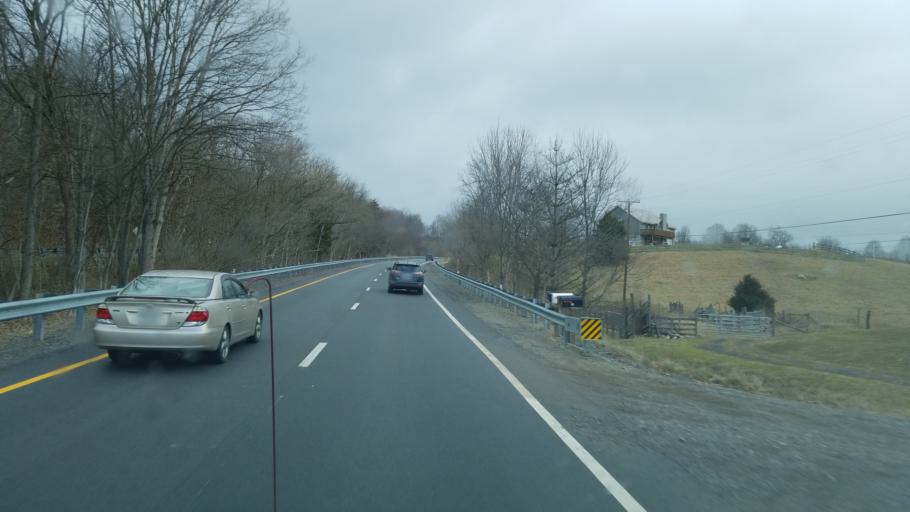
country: US
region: Virginia
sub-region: Giles County
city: Pearisburg
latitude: 37.2919
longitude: -80.7412
